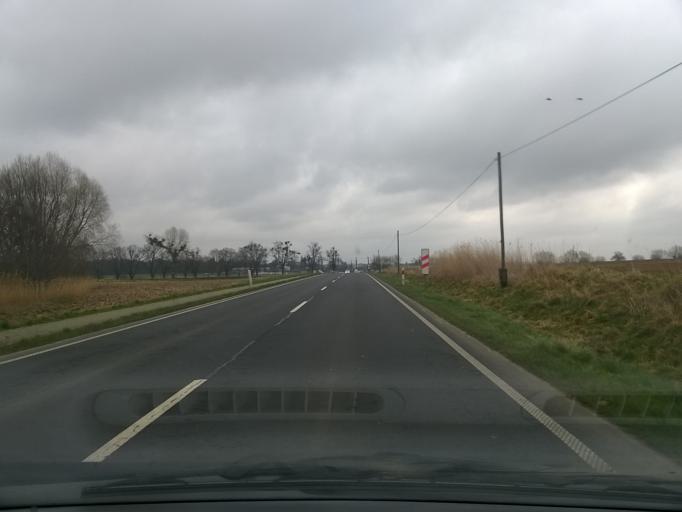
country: PL
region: Kujawsko-Pomorskie
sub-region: Powiat nakielski
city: Kcynia
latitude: 52.9894
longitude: 17.5807
